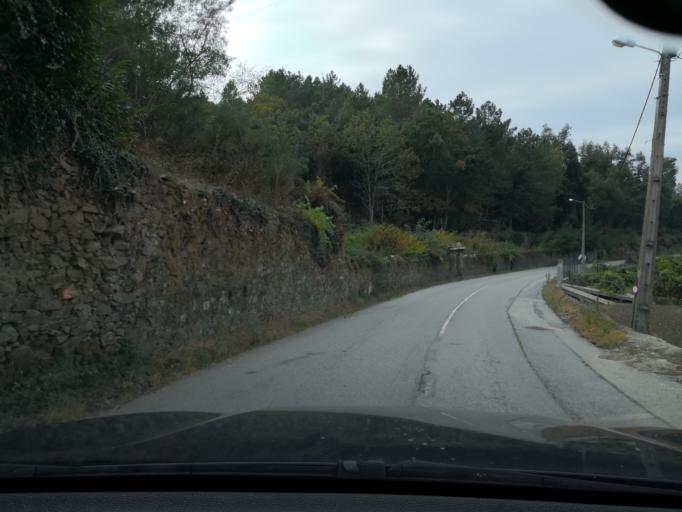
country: PT
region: Vila Real
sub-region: Peso da Regua
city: Peso da Regua
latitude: 41.1981
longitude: -7.7167
